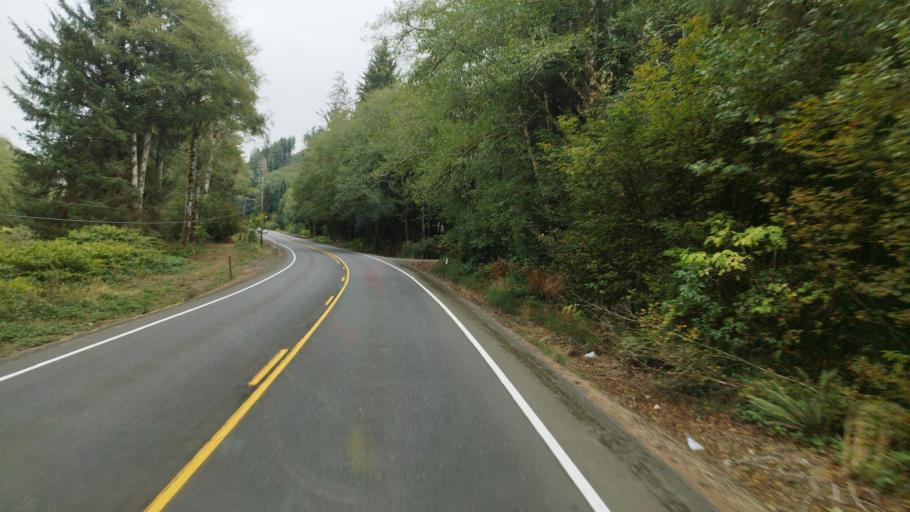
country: US
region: Oregon
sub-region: Clatsop County
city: Cannon Beach
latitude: 45.9088
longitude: -123.8835
